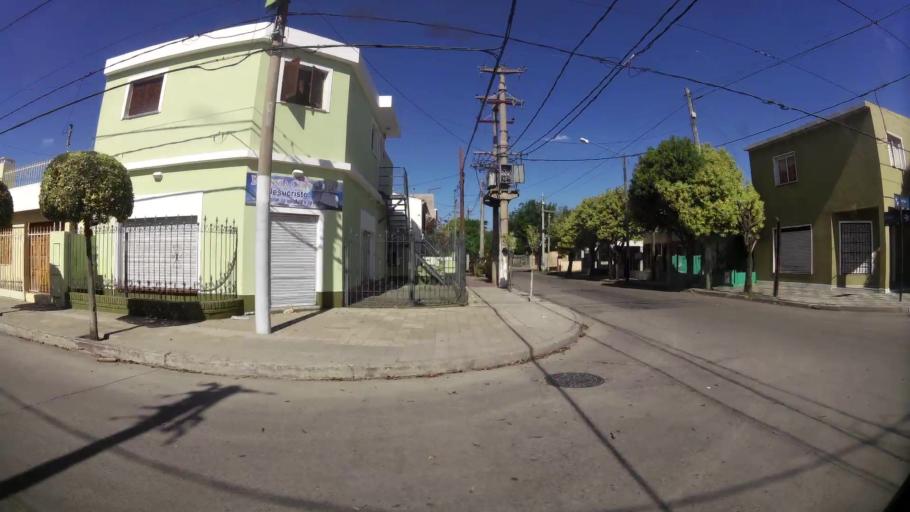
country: AR
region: Cordoba
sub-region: Departamento de Capital
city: Cordoba
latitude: -31.3725
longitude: -64.1818
